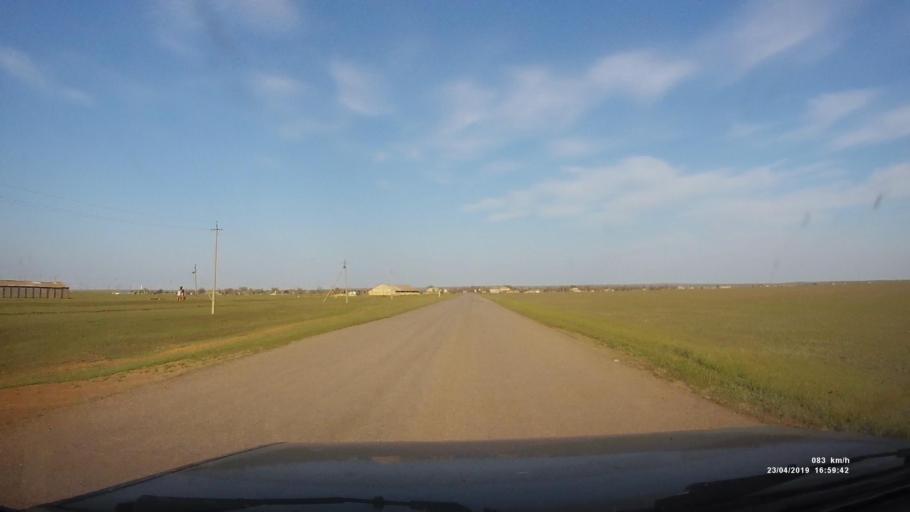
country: RU
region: Kalmykiya
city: Priyutnoye
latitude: 46.3086
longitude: 43.3945
